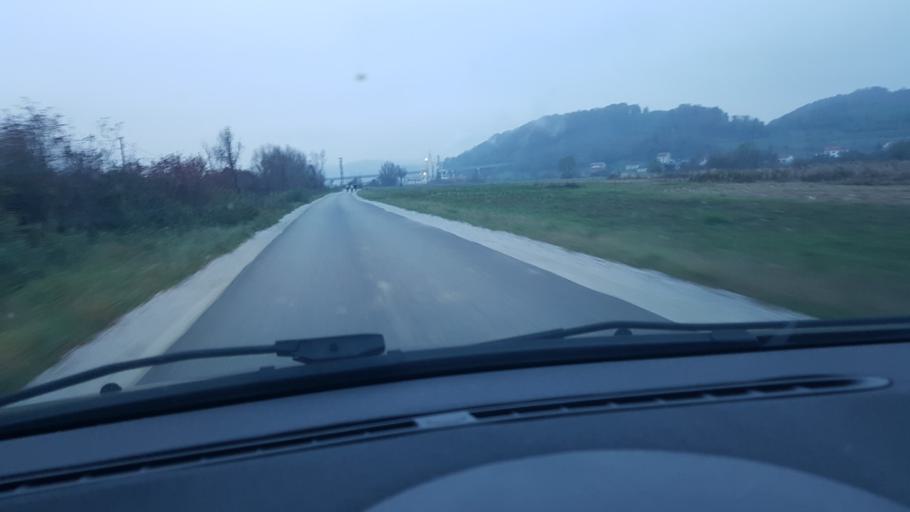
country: HR
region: Krapinsko-Zagorska
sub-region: Grad Krapina
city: Krapina
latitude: 46.1401
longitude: 15.8765
